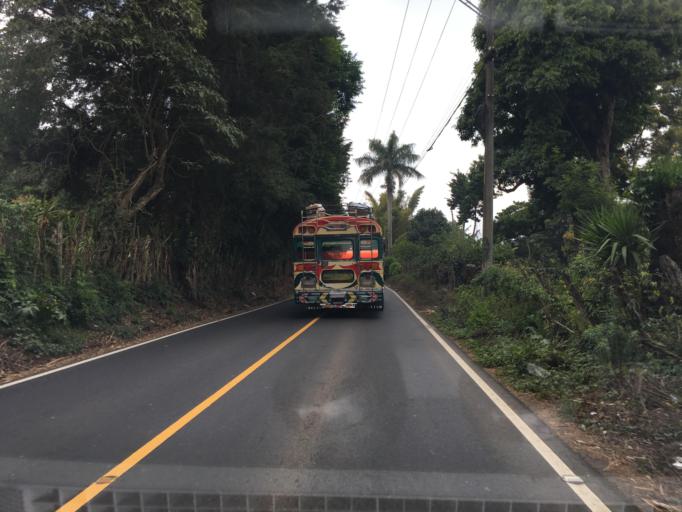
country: GT
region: Guatemala
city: Villa Canales
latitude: 14.4276
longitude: -90.5198
